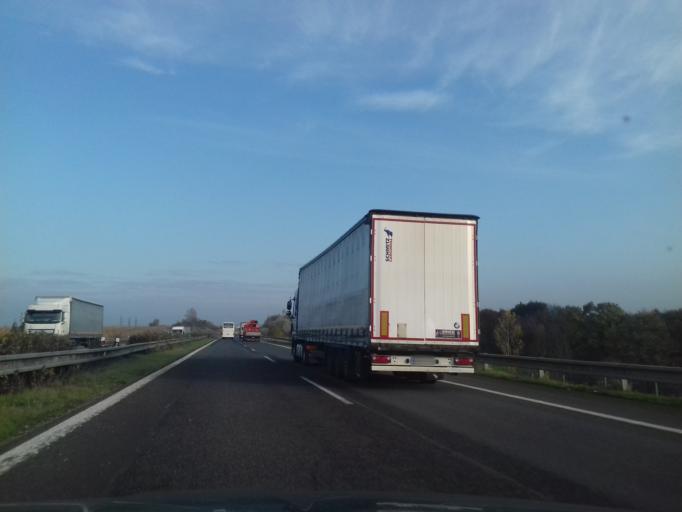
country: SK
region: Bratislavsky
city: Stupava
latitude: 48.2796
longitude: 17.0090
